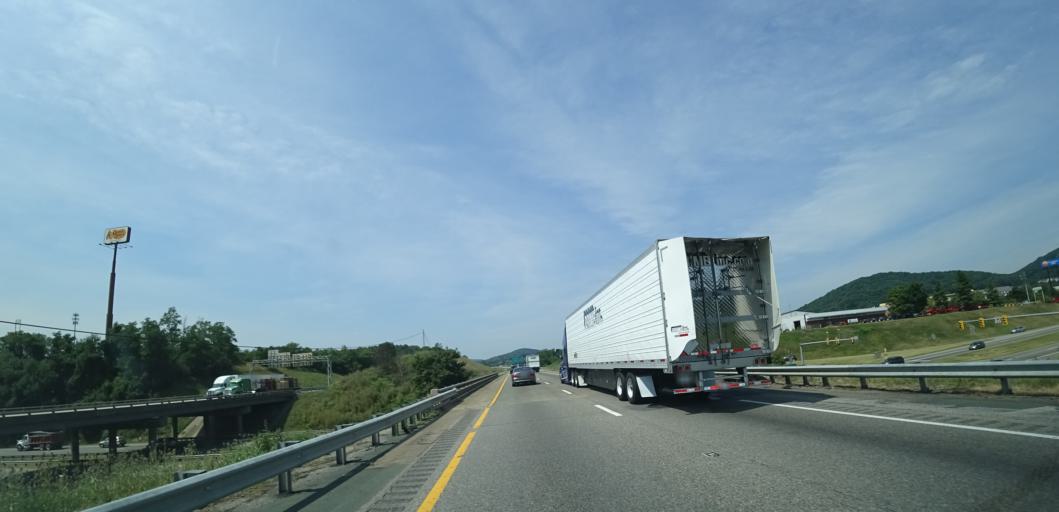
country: US
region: Virginia
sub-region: City of Staunton
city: Staunton
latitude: 38.1291
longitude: -79.0361
